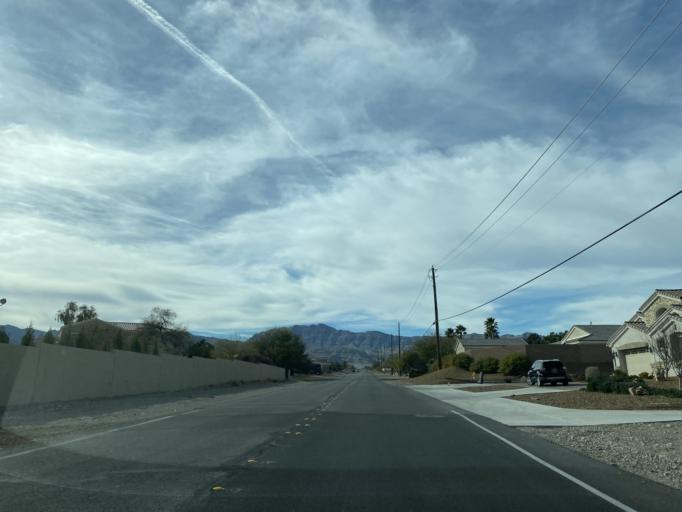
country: US
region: Nevada
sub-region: Clark County
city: Summerlin South
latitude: 36.2700
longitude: -115.3092
